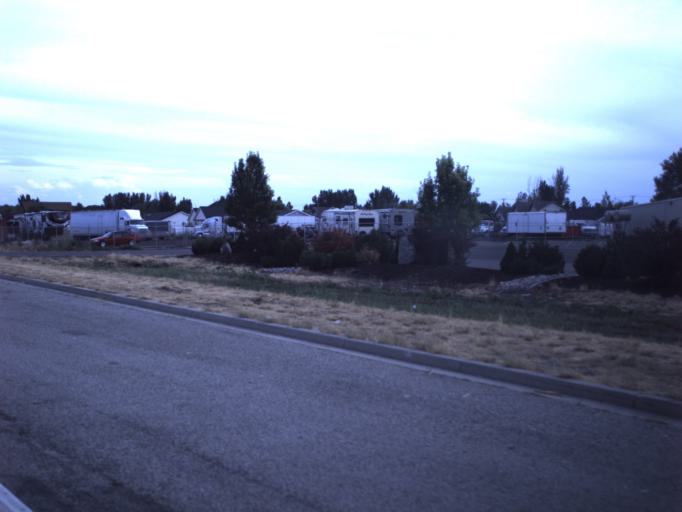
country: US
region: Utah
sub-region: Weber County
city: Farr West
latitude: 41.3225
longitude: -112.0306
